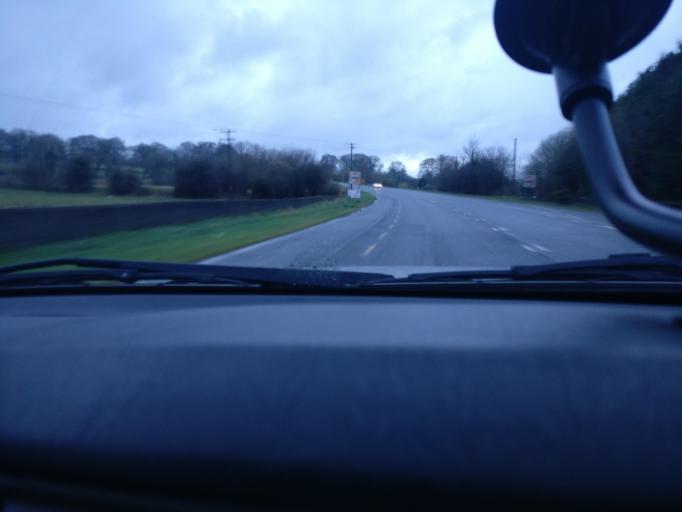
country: IE
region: Connaught
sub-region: County Galway
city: Ballinasloe
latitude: 53.3045
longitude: -8.3071
